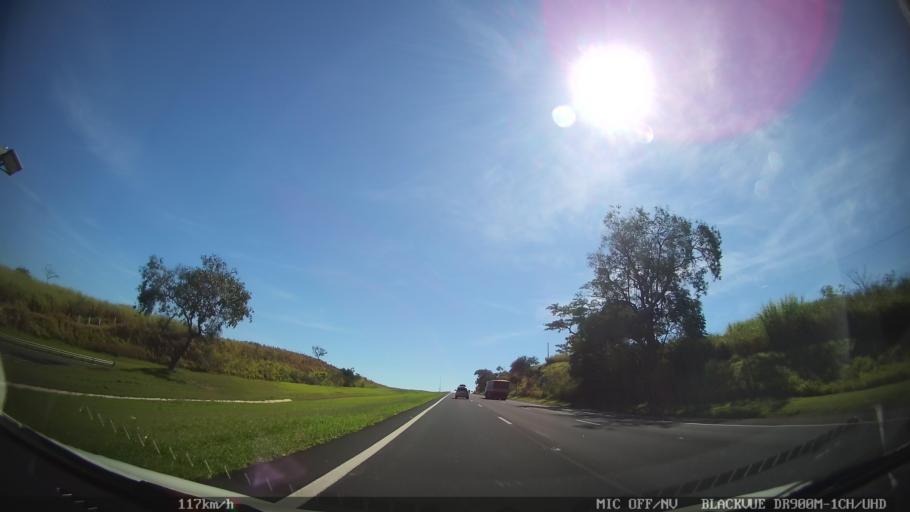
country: BR
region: Sao Paulo
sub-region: Santa Rita Do Passa Quatro
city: Santa Rita do Passa Quatro
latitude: -21.7032
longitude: -47.5949
